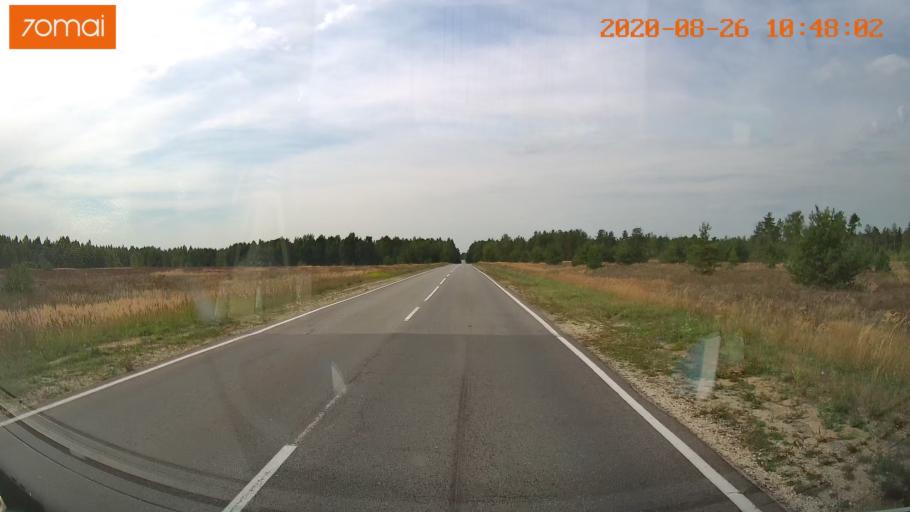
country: RU
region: Rjazan
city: Lashma
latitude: 54.7196
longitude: 41.1802
